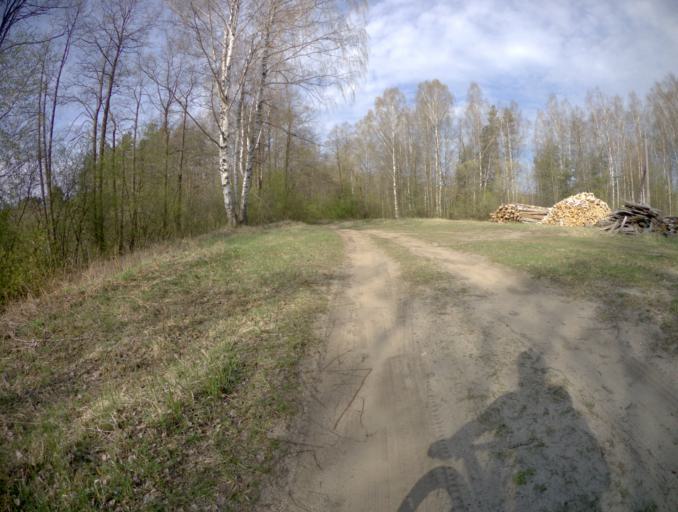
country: RU
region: Vladimir
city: Mezinovskiy
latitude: 55.6002
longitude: 40.3887
